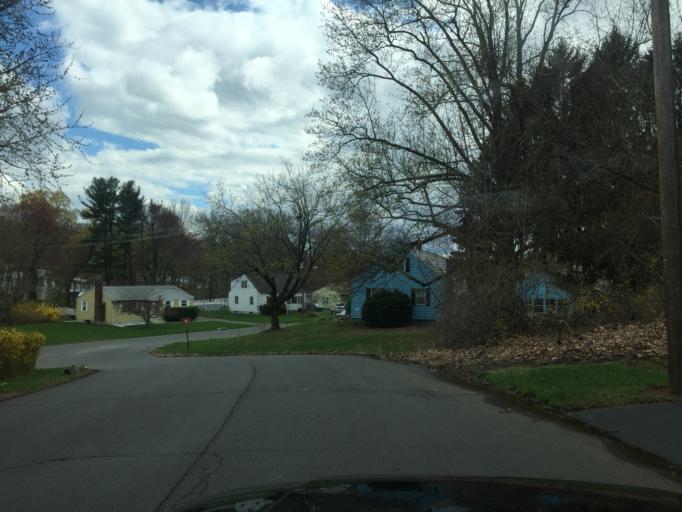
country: US
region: Connecticut
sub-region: Hartford County
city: New Britain
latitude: 41.7047
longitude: -72.7861
